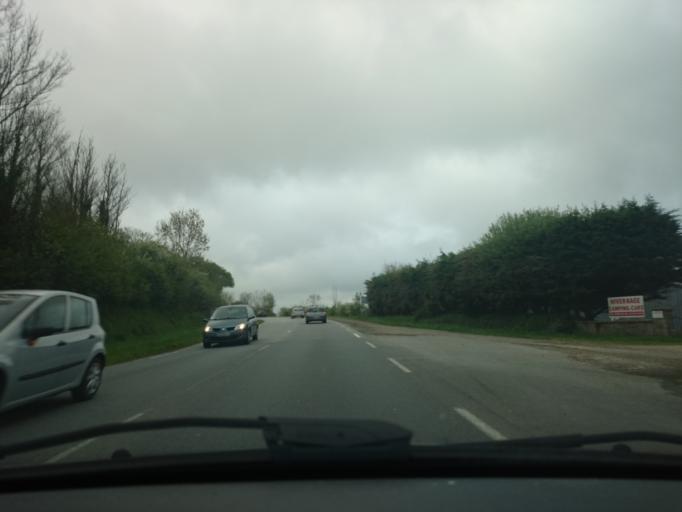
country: FR
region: Brittany
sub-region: Departement du Finistere
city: Saint-Renan
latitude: 48.4317
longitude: -4.6095
